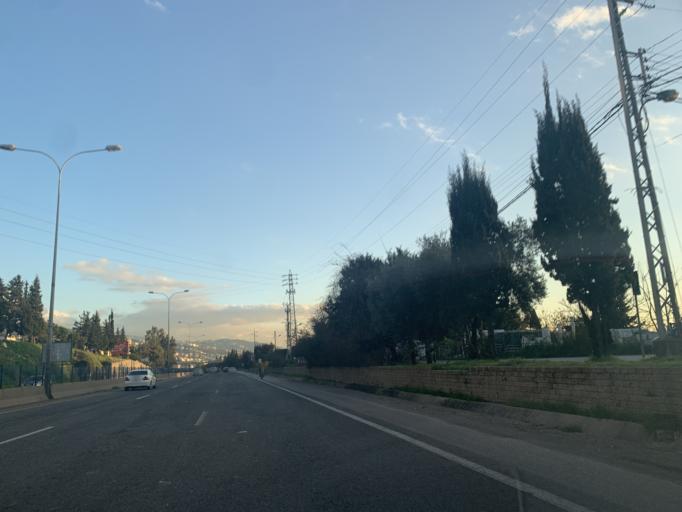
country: LB
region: Mont-Liban
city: Jbail
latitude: 34.1181
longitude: 35.6516
